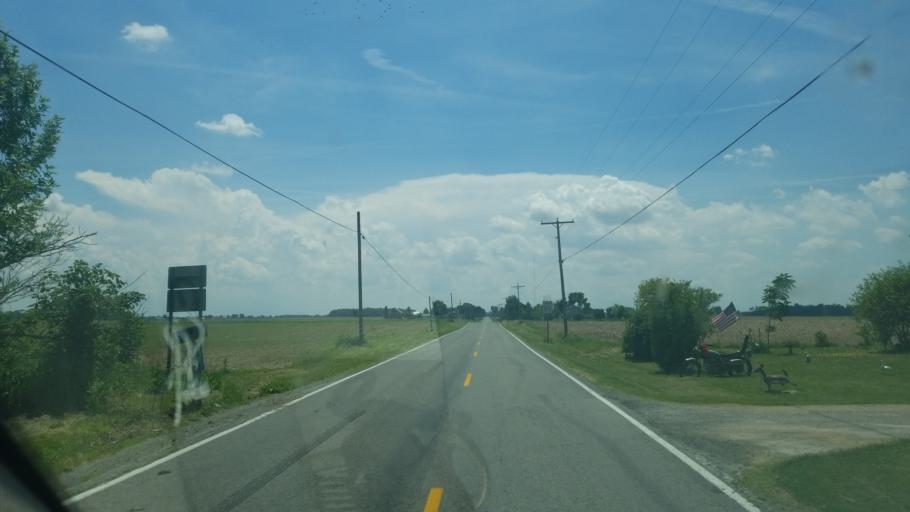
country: US
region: Ohio
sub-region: Hancock County
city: Arlington
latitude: 40.9317
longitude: -83.5945
